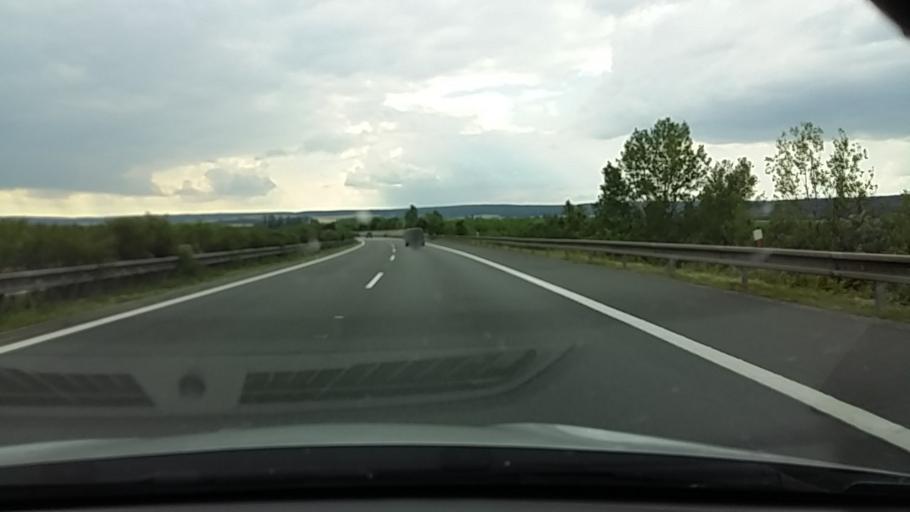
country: CZ
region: Plzensky
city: Nyrany
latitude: 49.7108
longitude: 13.1711
